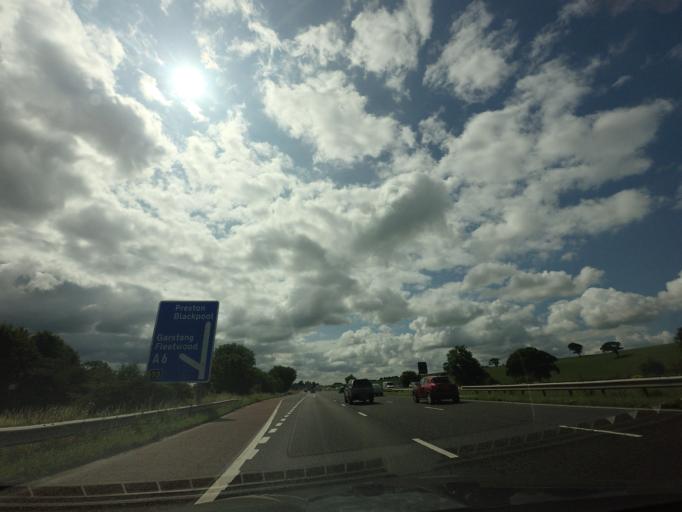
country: GB
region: England
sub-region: Lancashire
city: Galgate
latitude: 53.9891
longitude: -2.7811
